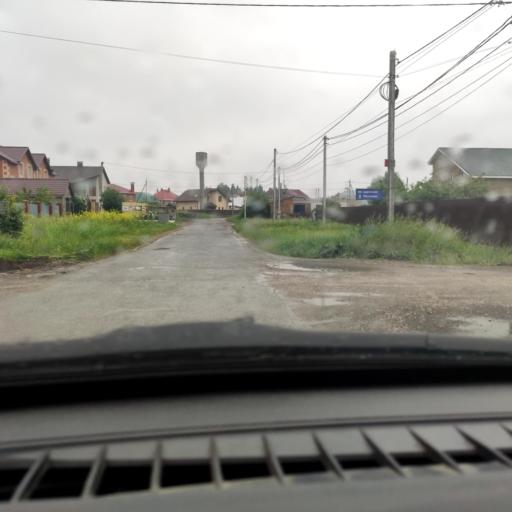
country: RU
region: Samara
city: Tol'yatti
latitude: 53.5661
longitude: 49.3803
